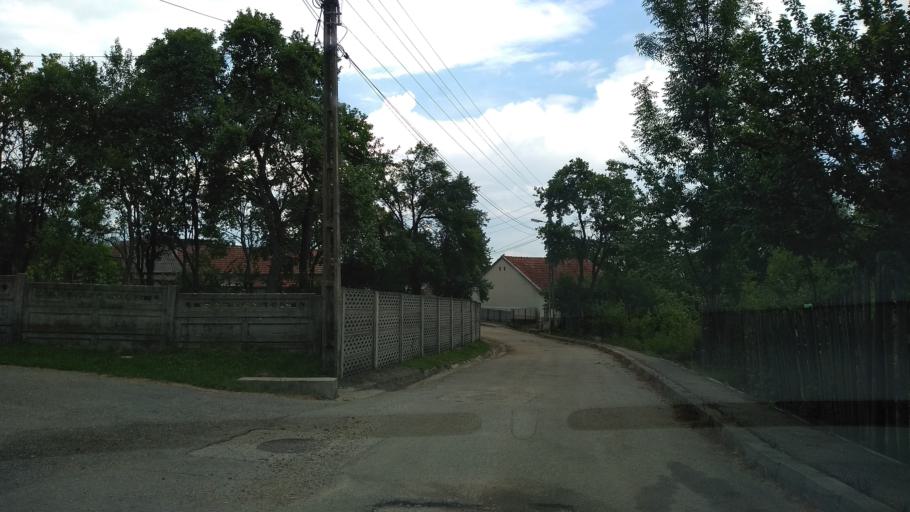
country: RO
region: Hunedoara
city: Salasu de Sus
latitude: 45.4859
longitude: 22.9460
